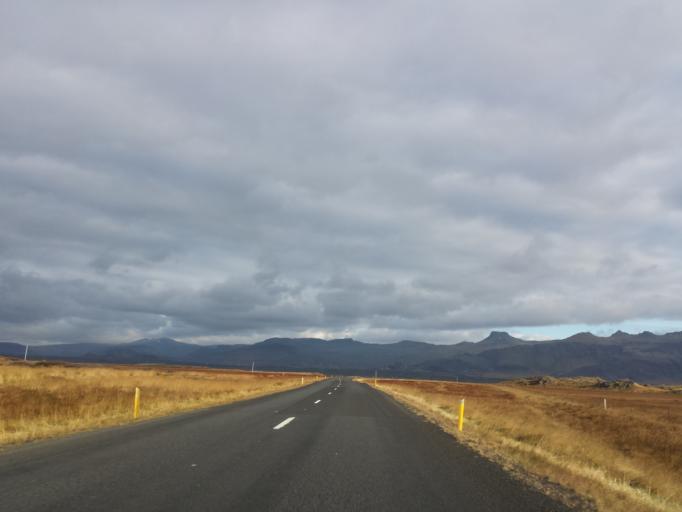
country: IS
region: West
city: Stykkisholmur
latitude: 64.8464
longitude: -22.3499
